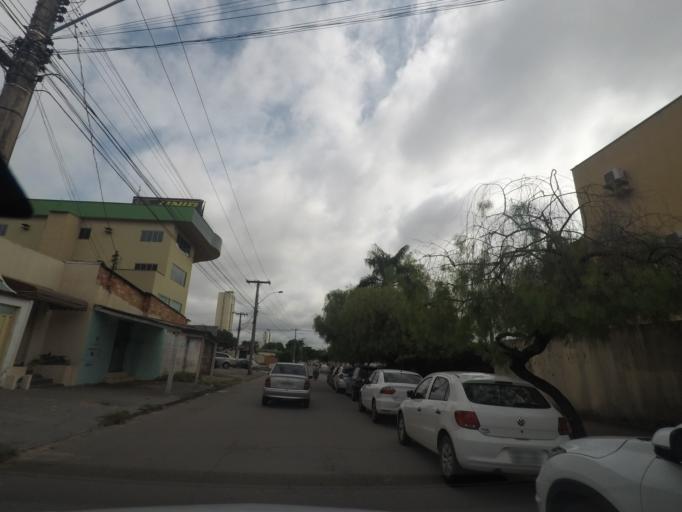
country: BR
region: Goias
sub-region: Goiania
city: Goiania
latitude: -16.7282
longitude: -49.2606
